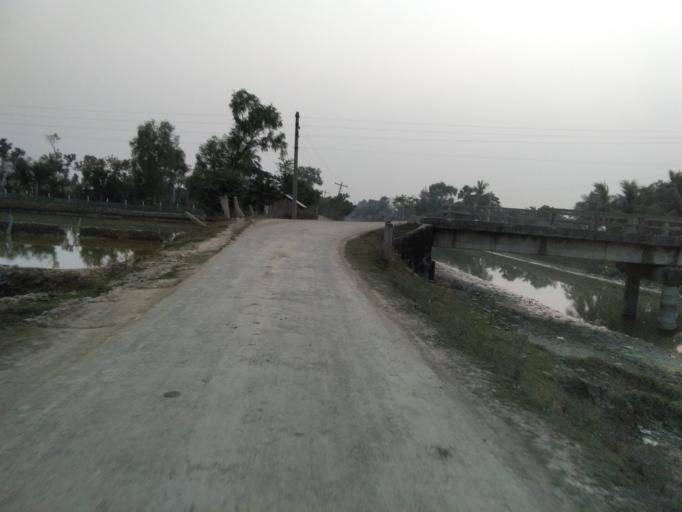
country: BD
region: Khulna
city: Satkhira
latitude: 22.6485
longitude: 89.0129
